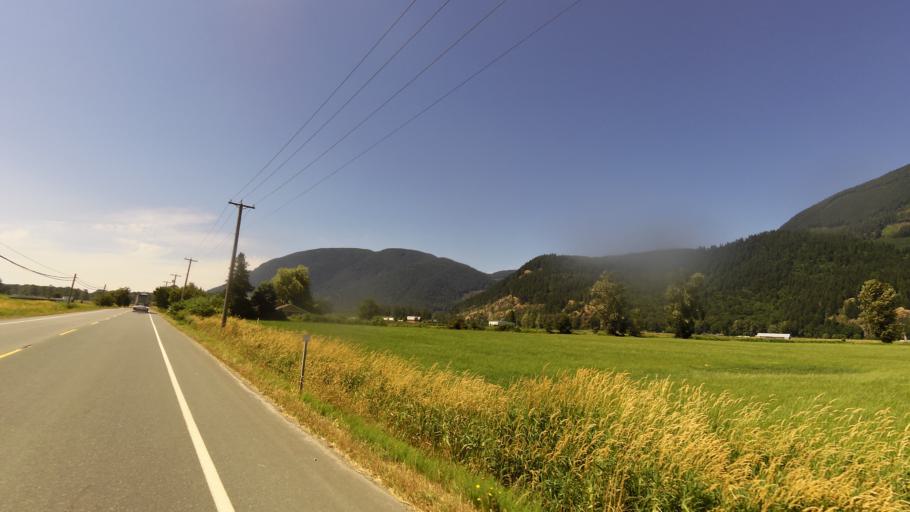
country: CA
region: British Columbia
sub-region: Fraser Valley Regional District
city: Chilliwack
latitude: 49.1693
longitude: -122.1204
